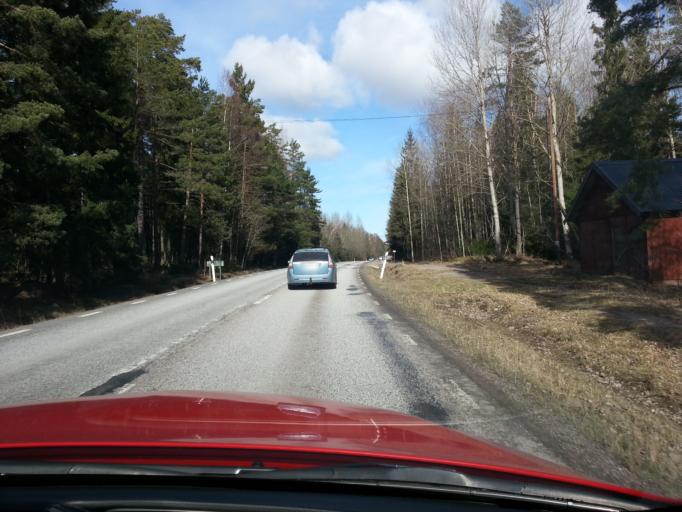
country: SE
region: Uppsala
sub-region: Osthammars Kommun
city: Gimo
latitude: 60.1072
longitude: 18.1252
